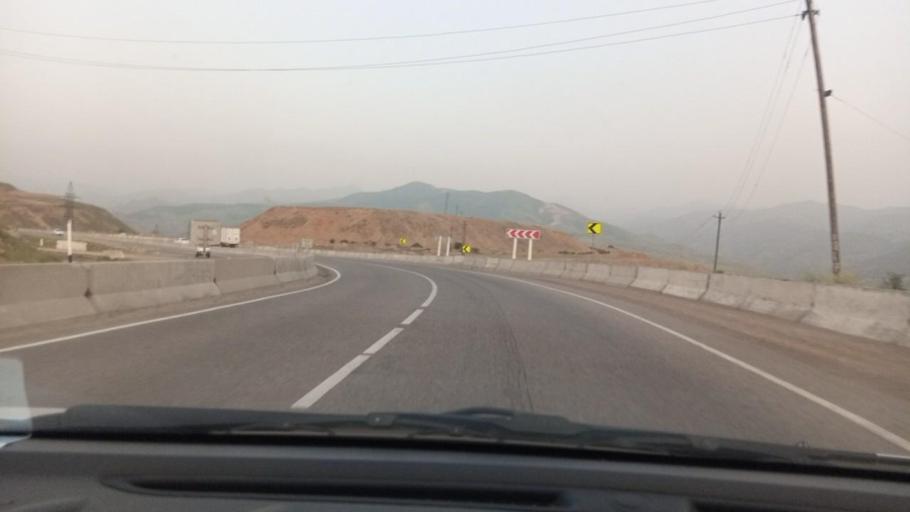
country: UZ
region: Toshkent
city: Angren
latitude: 41.0597
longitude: 70.1871
